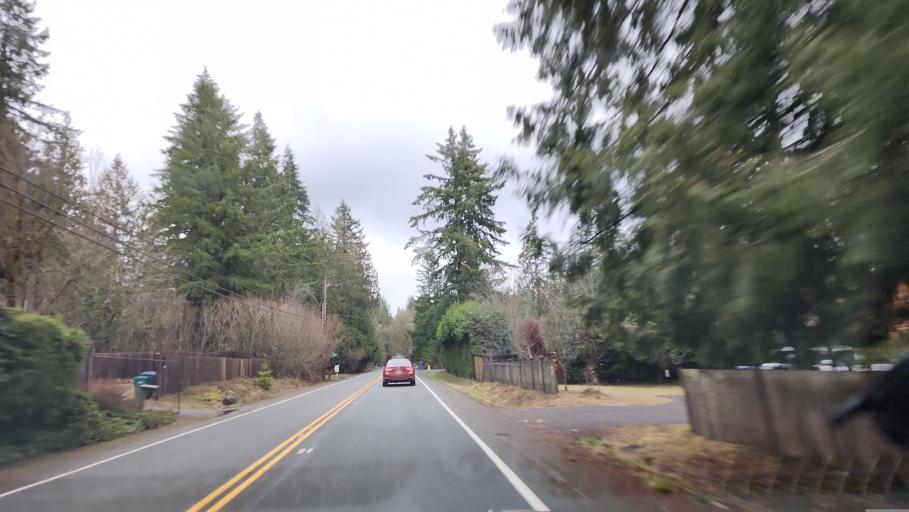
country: US
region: Washington
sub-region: King County
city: Cottage Lake
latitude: 47.7434
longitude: -122.0682
